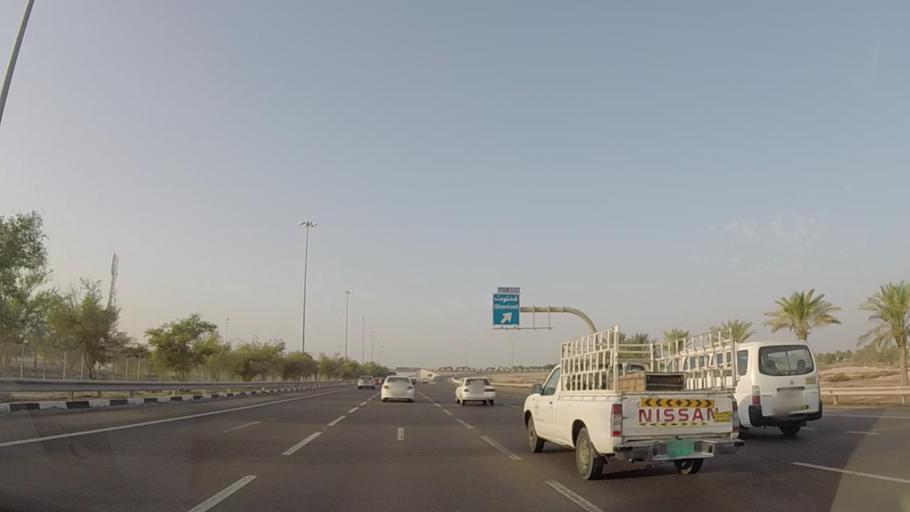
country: AE
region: Dubai
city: Dubai
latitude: 24.8635
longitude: 54.9097
